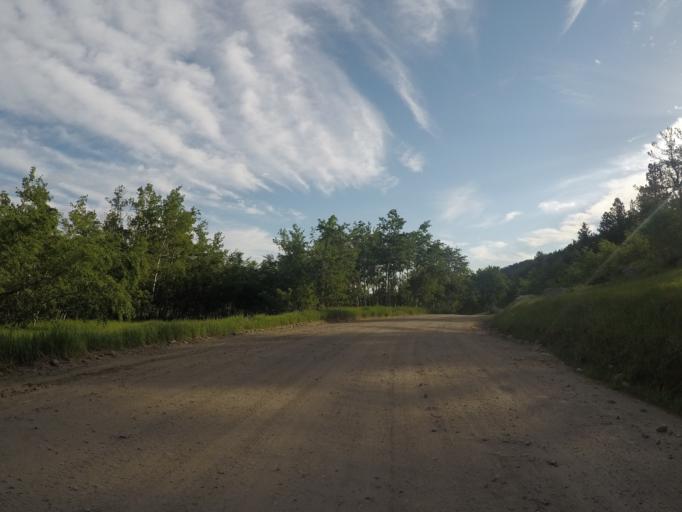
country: US
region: Montana
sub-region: Stillwater County
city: Absarokee
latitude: 45.2858
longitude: -109.5425
